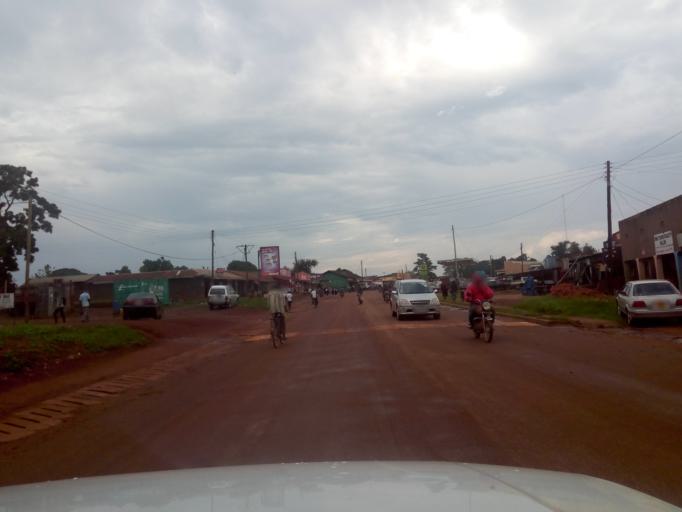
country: UG
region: Western Region
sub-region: Masindi District
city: Masindi
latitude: 1.6933
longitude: 31.7093
